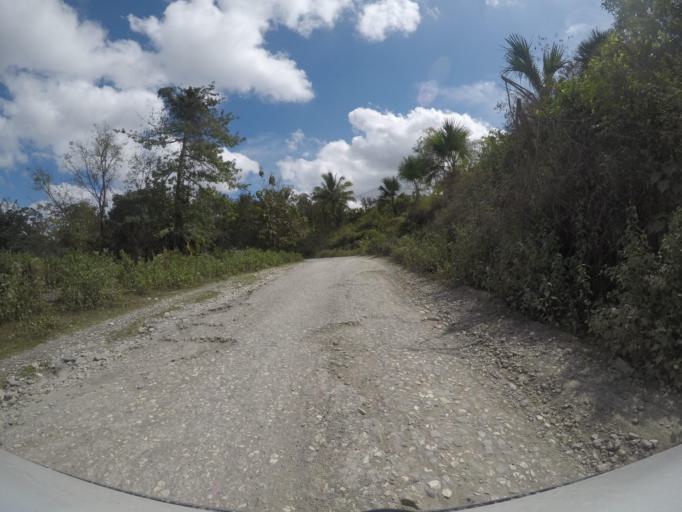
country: TL
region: Viqueque
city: Viqueque
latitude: -8.8687
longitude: 126.3422
